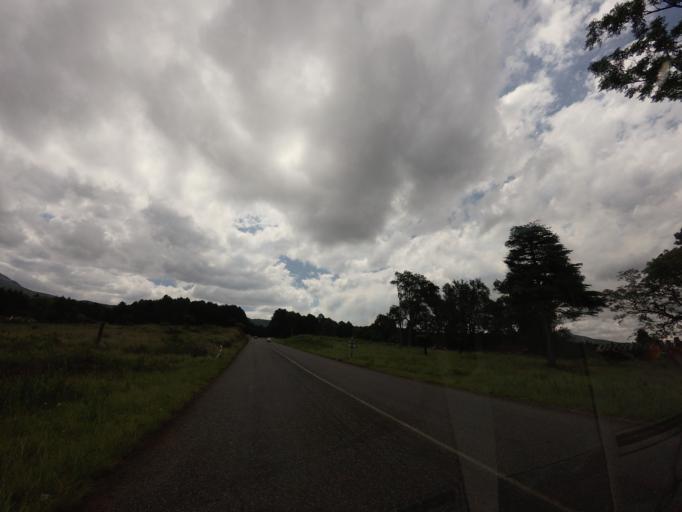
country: ZA
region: Mpumalanga
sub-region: Ehlanzeni District
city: Graksop
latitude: -24.9828
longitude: 30.8139
